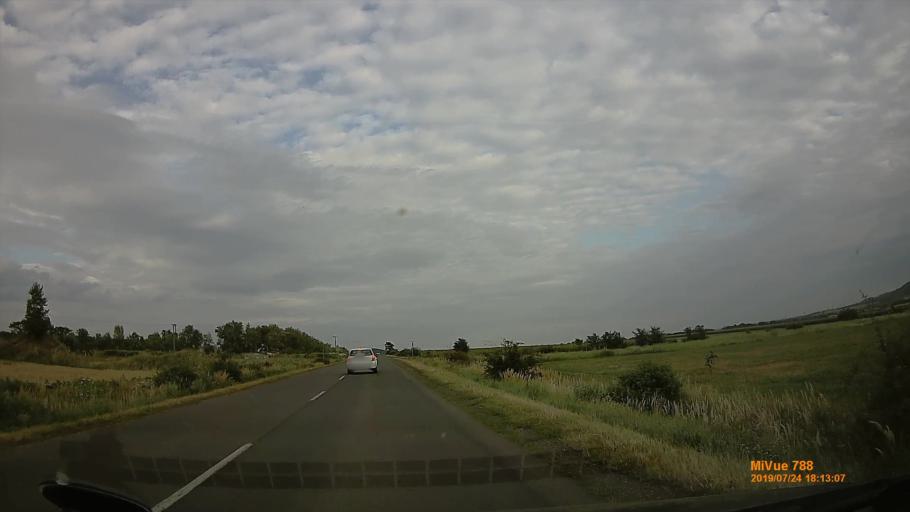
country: HU
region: Borsod-Abauj-Zemplen
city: Tallya
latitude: 48.2312
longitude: 21.2165
